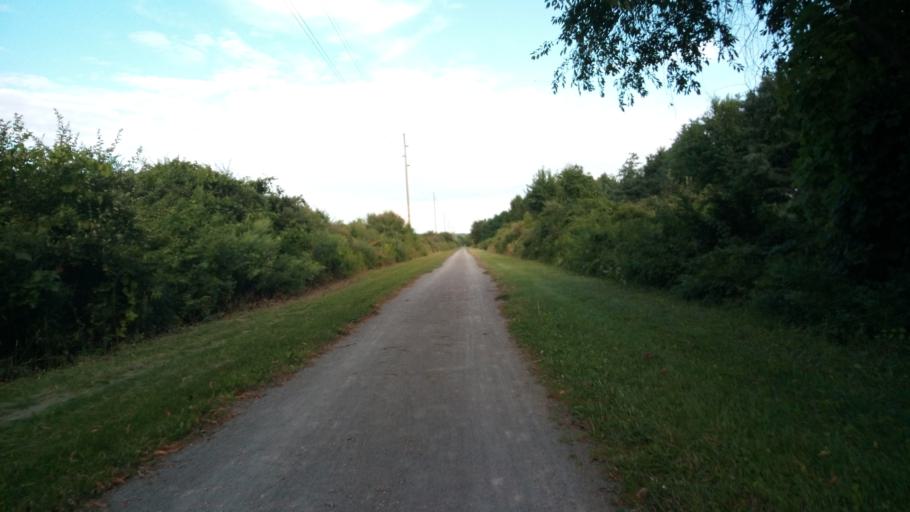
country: US
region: New York
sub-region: Ontario County
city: Victor
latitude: 43.0027
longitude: -77.4798
